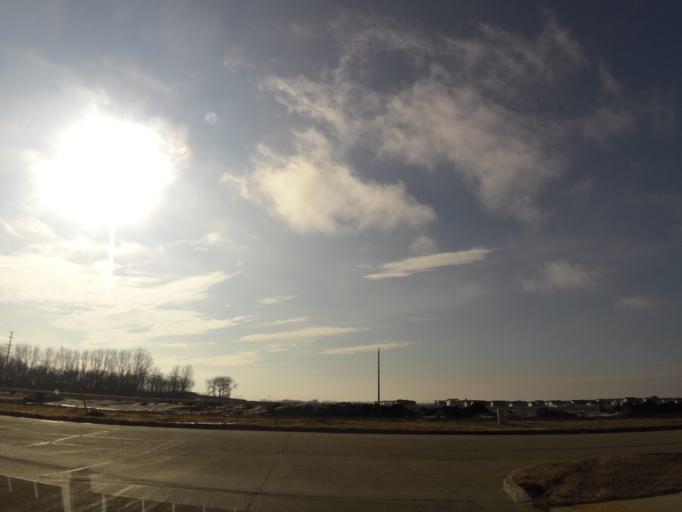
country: US
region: North Dakota
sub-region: Grand Forks County
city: Grand Forks
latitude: 47.8778
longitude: -97.0640
